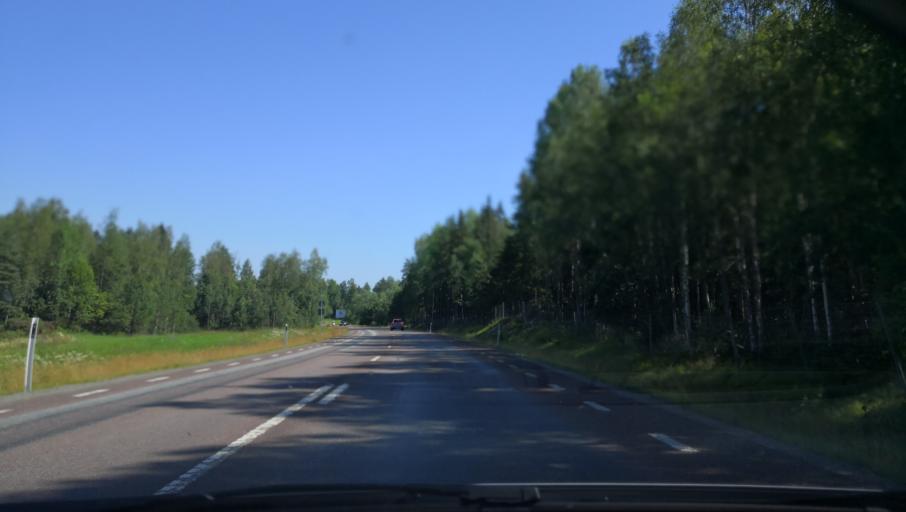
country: SE
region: Gaevleborg
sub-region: Ovanakers Kommun
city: Alfta
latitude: 61.3371
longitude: 16.0381
